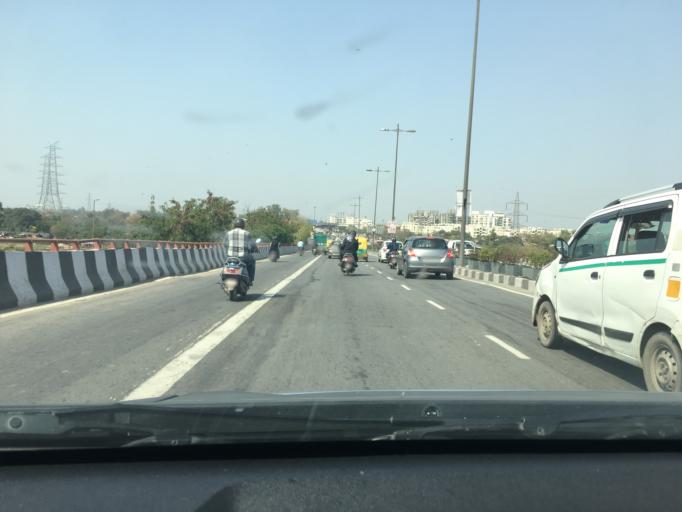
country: IN
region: NCT
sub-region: North Delhi
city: Delhi
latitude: 28.6444
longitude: 77.2689
